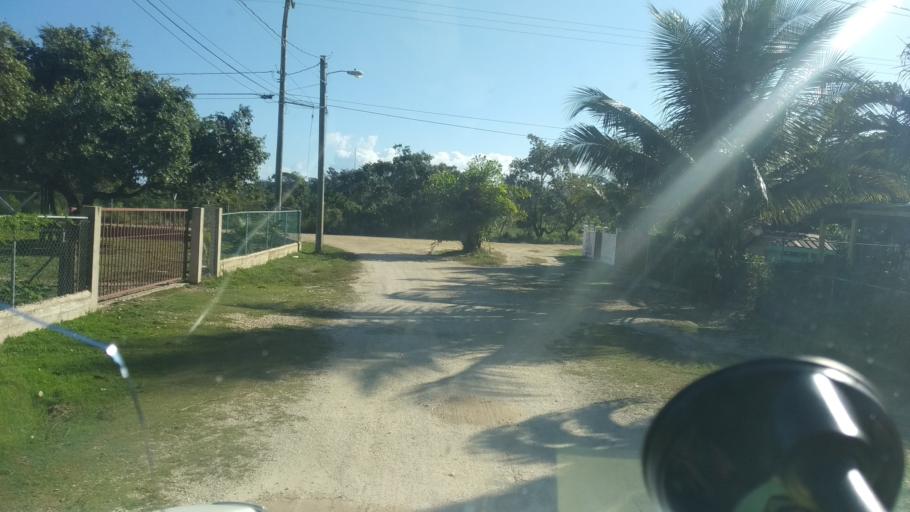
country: BZ
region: Belize
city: Belize City
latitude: 17.5573
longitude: -88.3274
